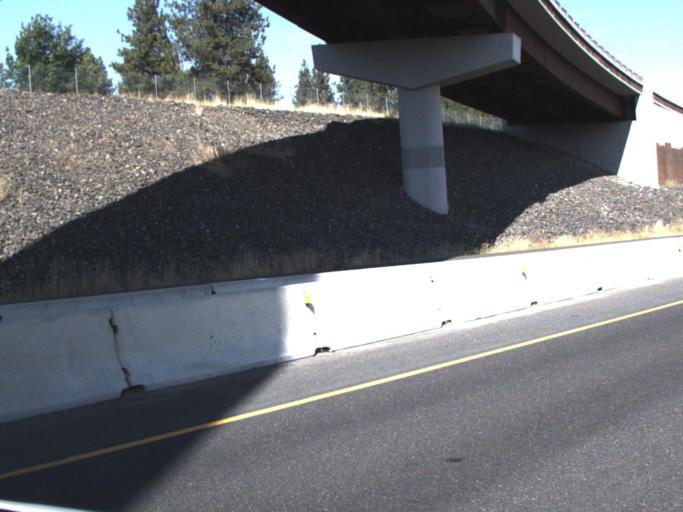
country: US
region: Washington
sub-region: Spokane County
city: Mead
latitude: 47.7758
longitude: -117.3721
